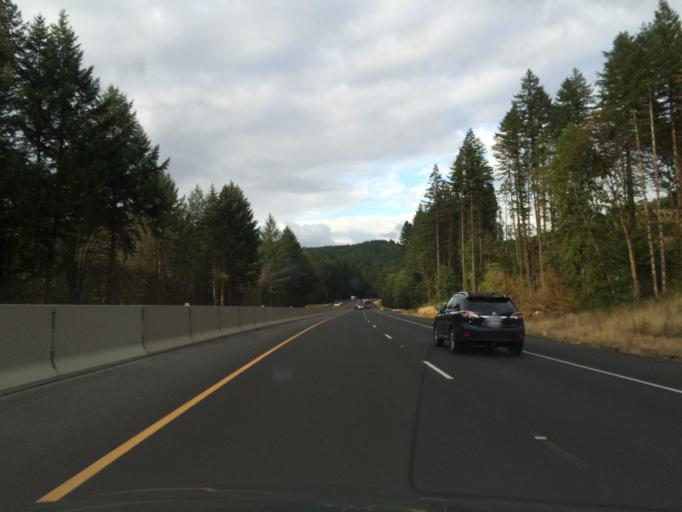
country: US
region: Oregon
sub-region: Lane County
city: Cottage Grove
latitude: 43.7461
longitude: -123.1802
